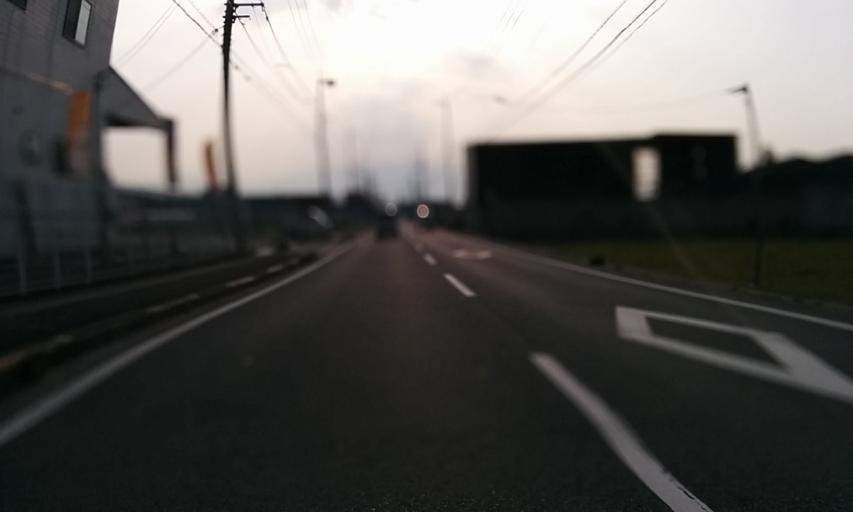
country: JP
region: Ehime
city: Saijo
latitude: 33.8947
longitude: 133.1538
